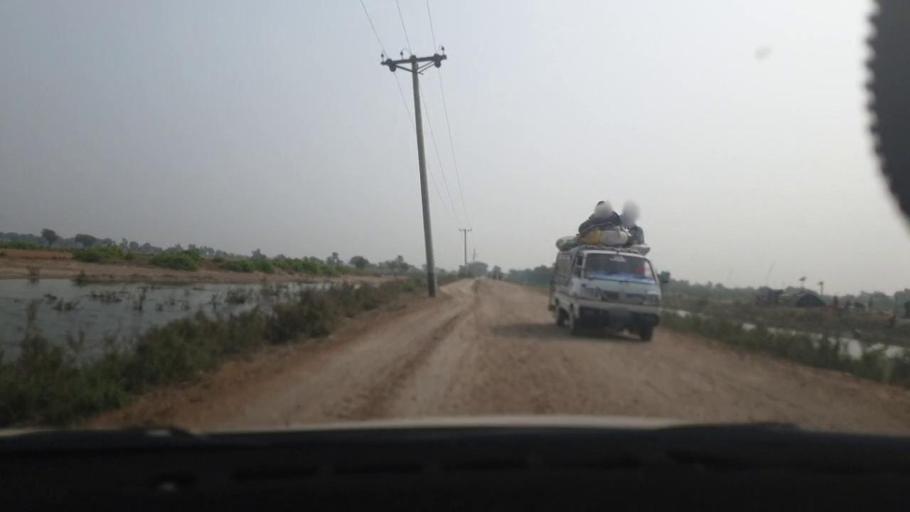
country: PK
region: Sindh
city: Tando Muhammad Khan
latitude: 25.0763
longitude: 68.4968
